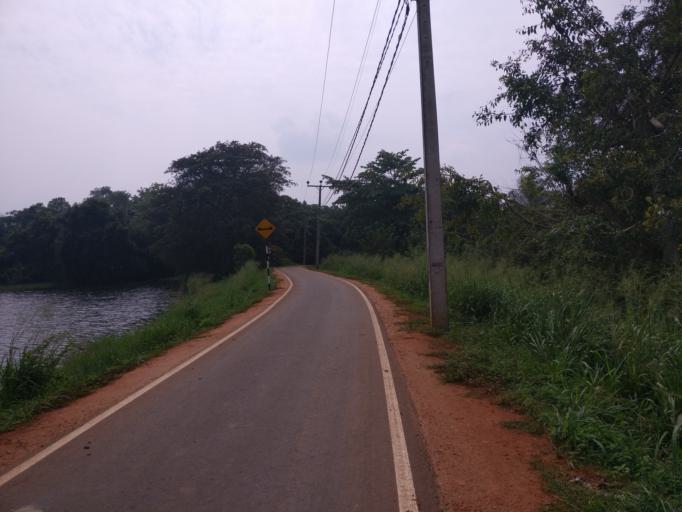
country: LK
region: Central
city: Dambulla
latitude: 7.8362
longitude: 80.6480
